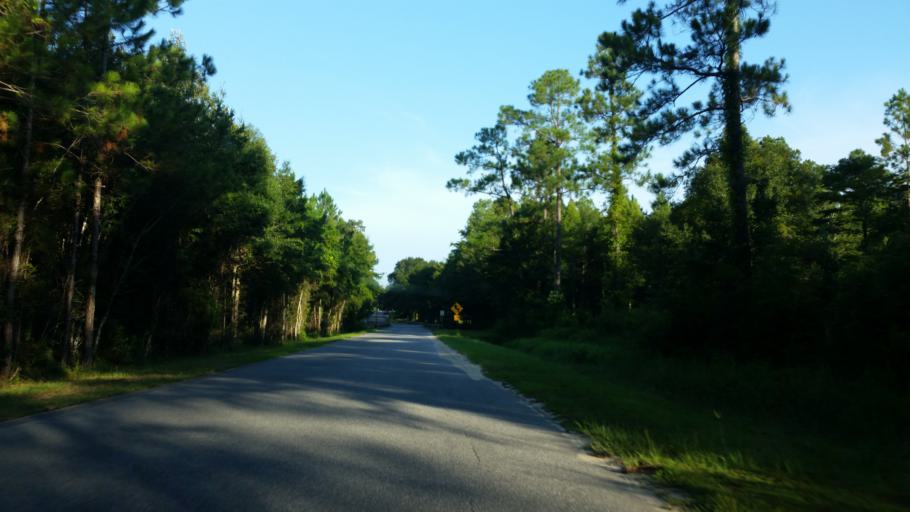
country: US
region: Florida
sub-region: Escambia County
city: Bellview
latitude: 30.4844
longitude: -87.3317
